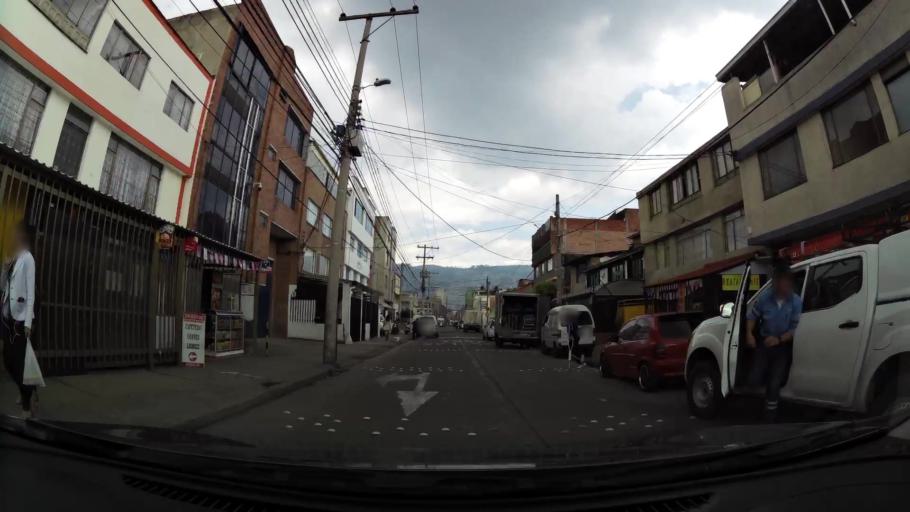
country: CO
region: Cundinamarca
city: La Calera
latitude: 4.7422
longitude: -74.0406
